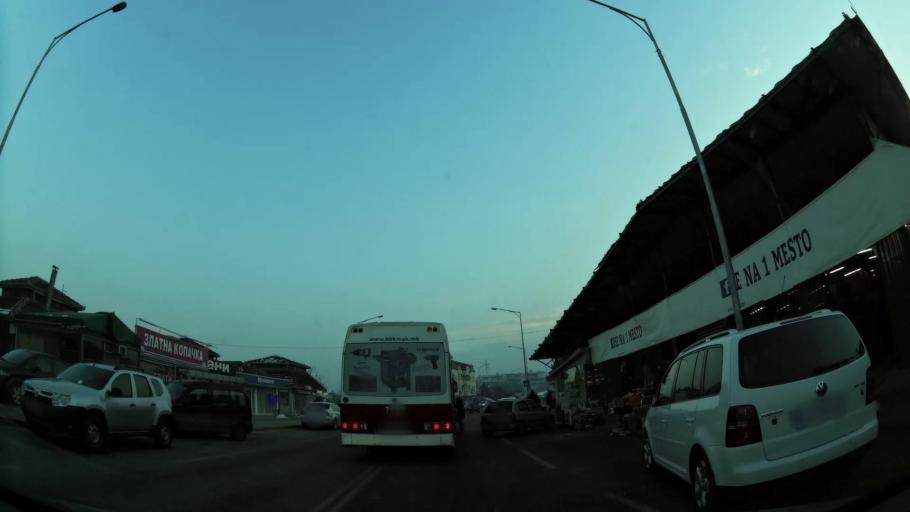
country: MK
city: Creshevo
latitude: 42.0047
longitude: 21.5041
